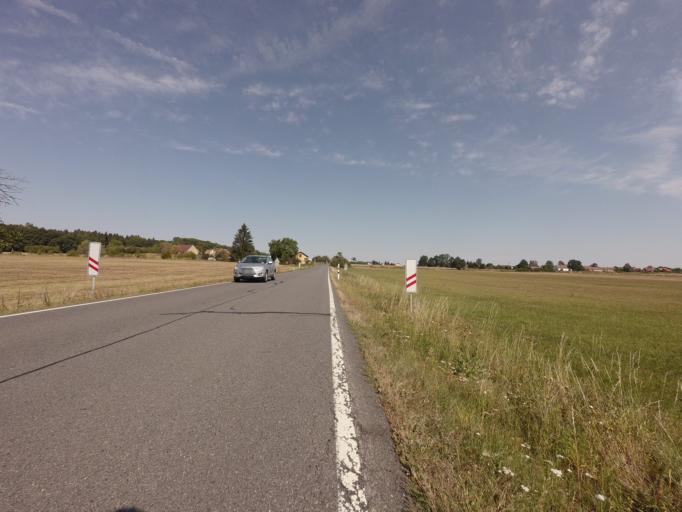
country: CZ
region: Jihocesky
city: Milevsko
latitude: 49.4082
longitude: 14.3611
